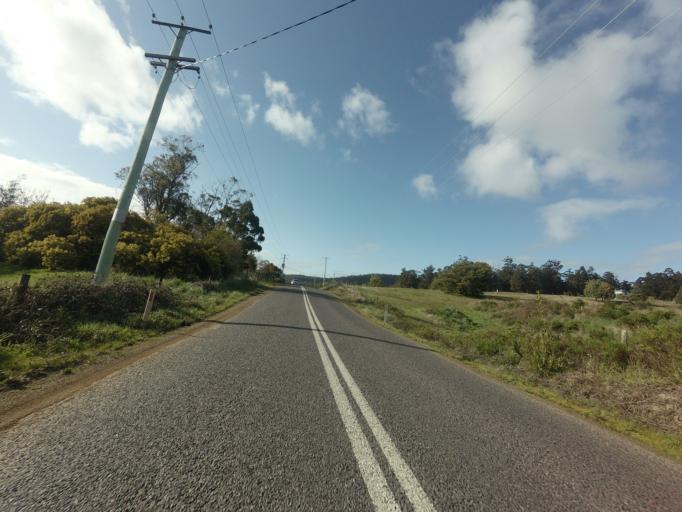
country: AU
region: Tasmania
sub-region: Huon Valley
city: Geeveston
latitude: -43.2123
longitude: 146.9867
